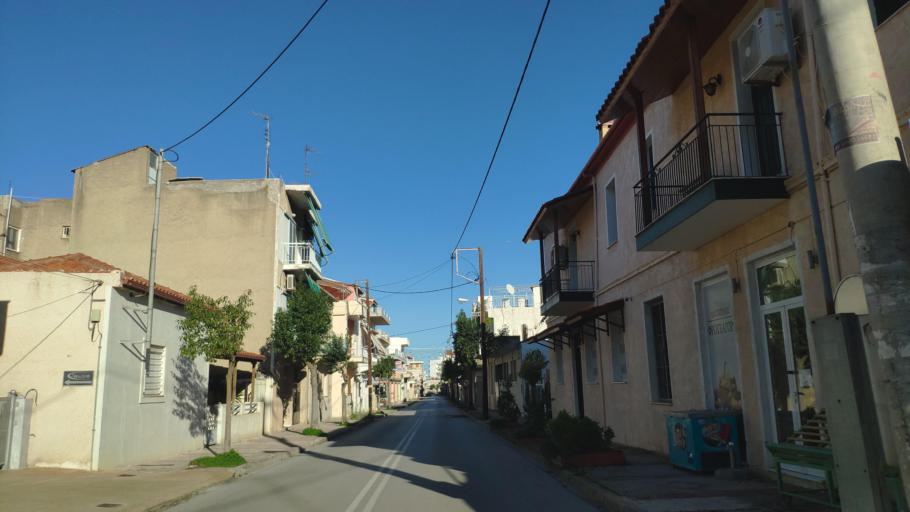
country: GR
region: Peloponnese
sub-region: Nomos Korinthias
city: Xylokastro
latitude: 38.0770
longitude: 22.6256
